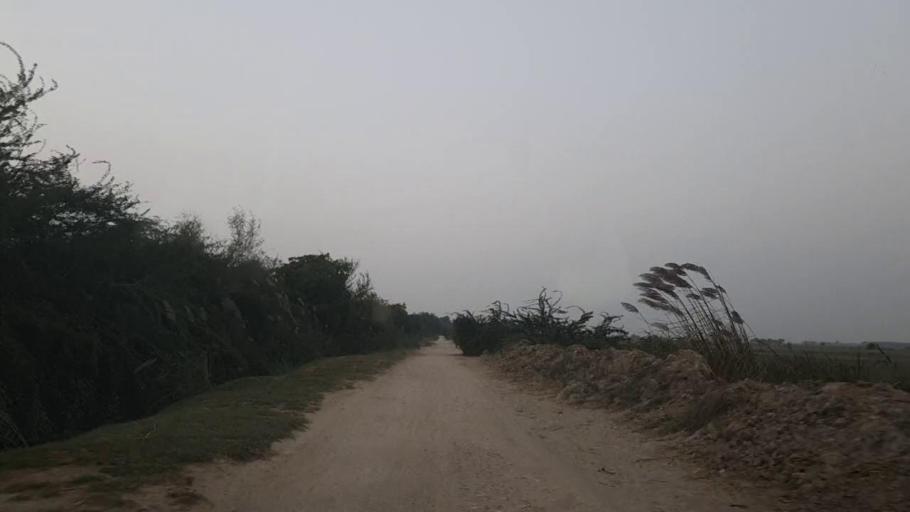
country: PK
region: Sindh
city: Mirpur Sakro
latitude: 24.5781
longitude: 67.7860
